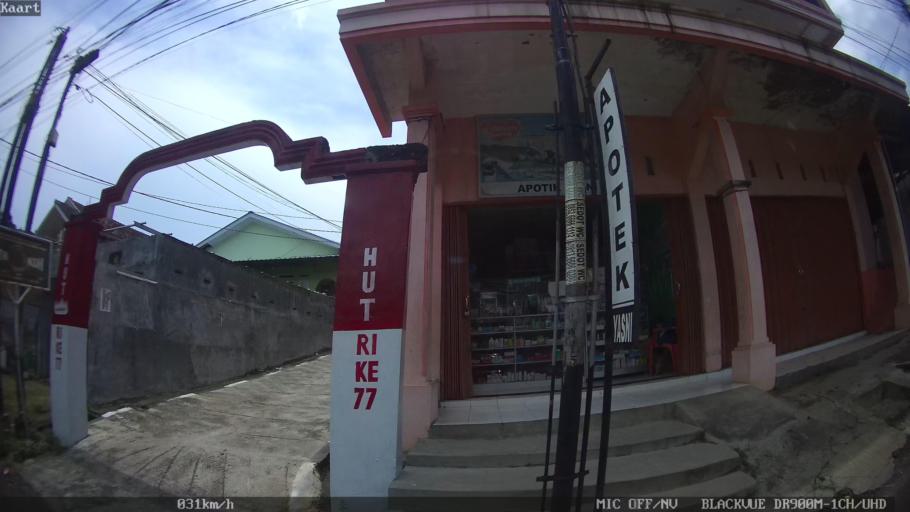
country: ID
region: Lampung
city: Bandarlampung
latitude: -5.4115
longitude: 105.2421
